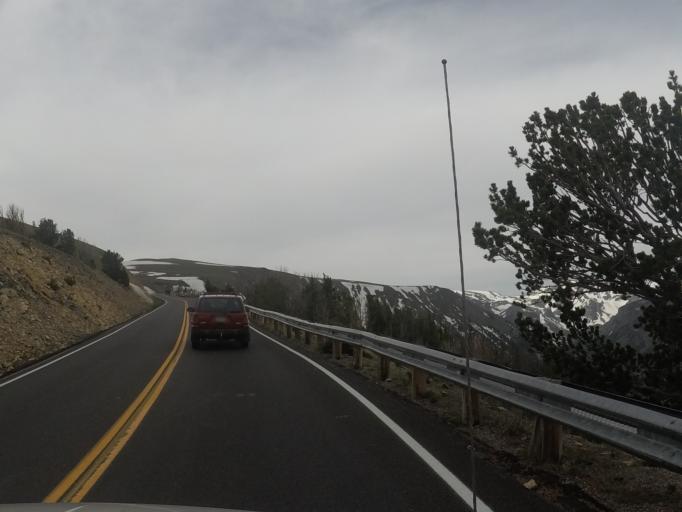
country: US
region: Montana
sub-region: Carbon County
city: Red Lodge
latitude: 45.0367
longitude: -109.4115
